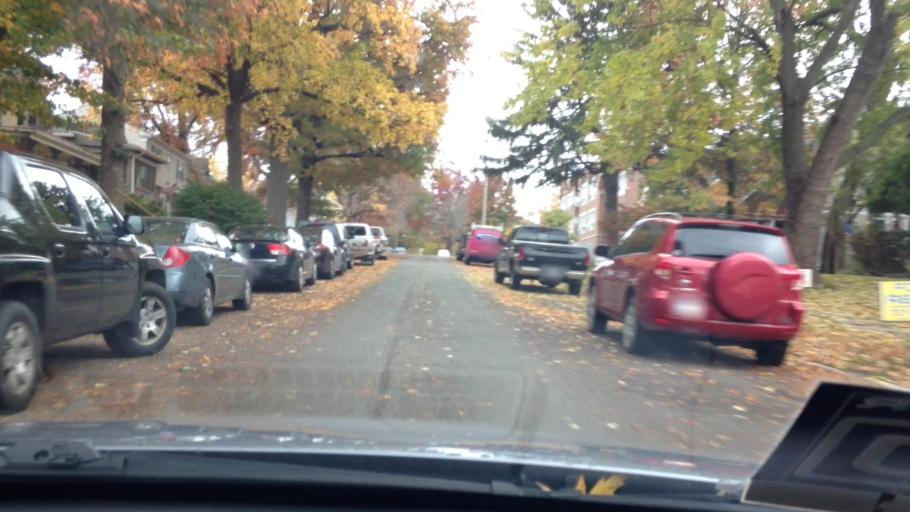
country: US
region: Kansas
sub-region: Leavenworth County
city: Leavenworth
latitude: 39.3101
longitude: -94.9148
